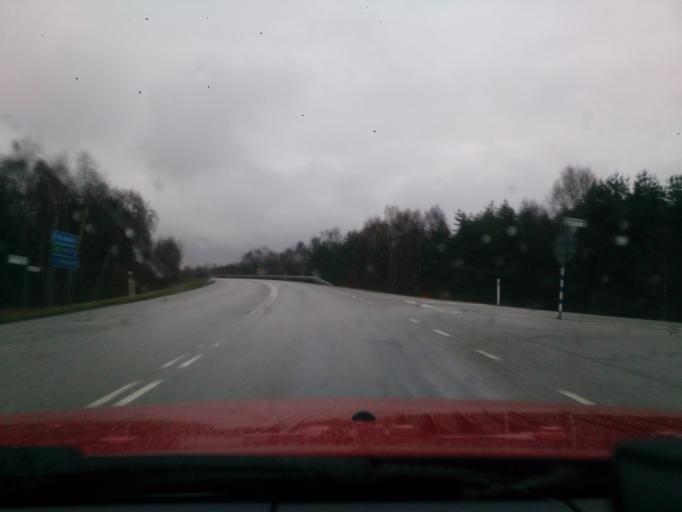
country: SE
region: Skane
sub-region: Ystads Kommun
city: Ystad
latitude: 55.4262
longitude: 13.7686
